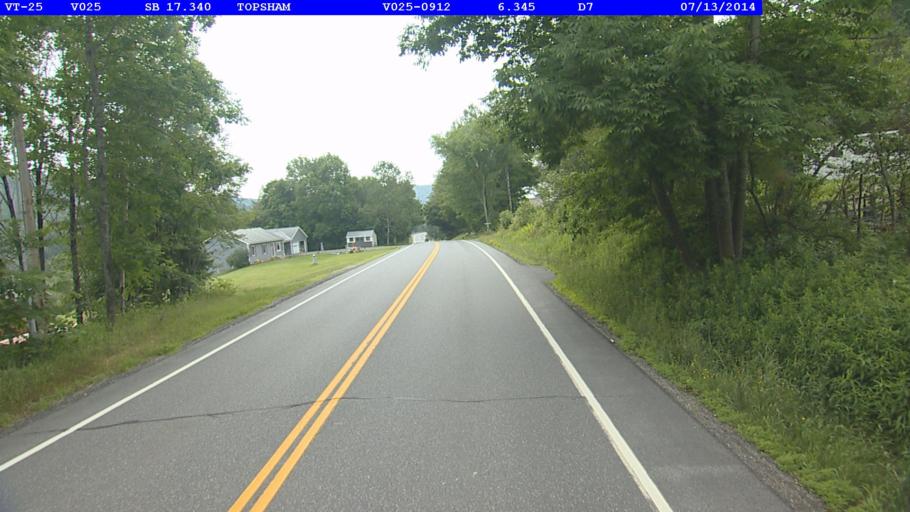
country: US
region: Vermont
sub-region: Washington County
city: South Barre
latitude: 44.1354
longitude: -72.3176
